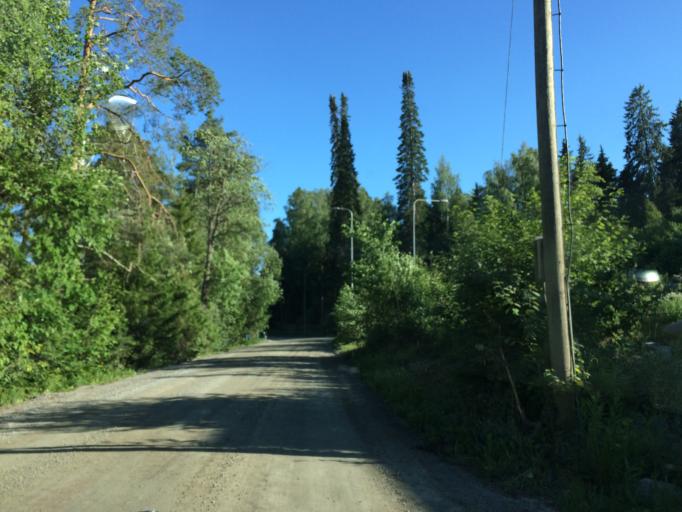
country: FI
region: Haeme
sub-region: Haemeenlinna
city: Haemeenlinna
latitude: 60.9897
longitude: 24.5058
